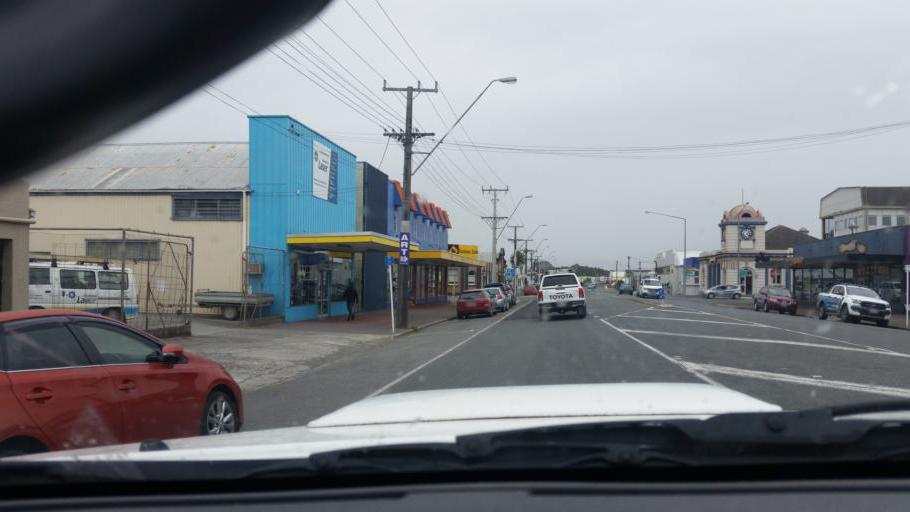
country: NZ
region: Northland
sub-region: Kaipara District
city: Dargaville
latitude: -35.9408
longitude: 173.8692
